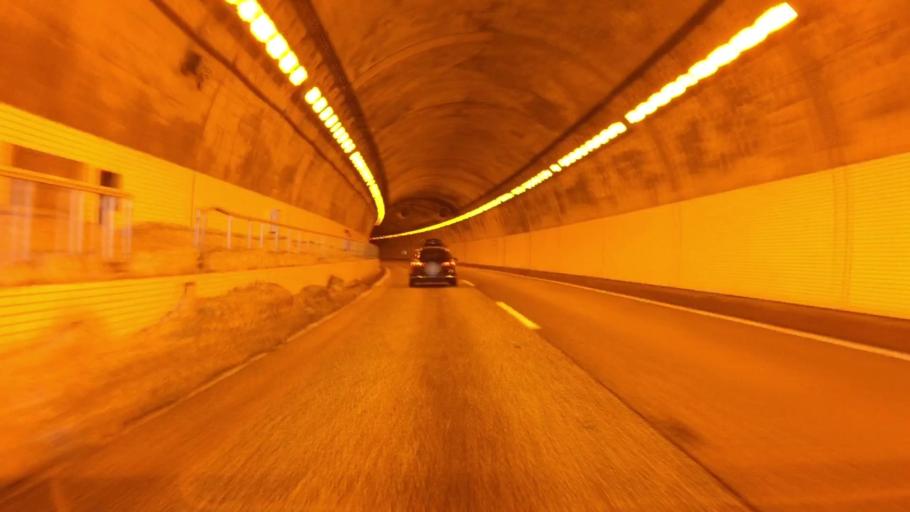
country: JP
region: Niigata
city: Shiozawa
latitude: 36.9757
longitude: 138.8093
